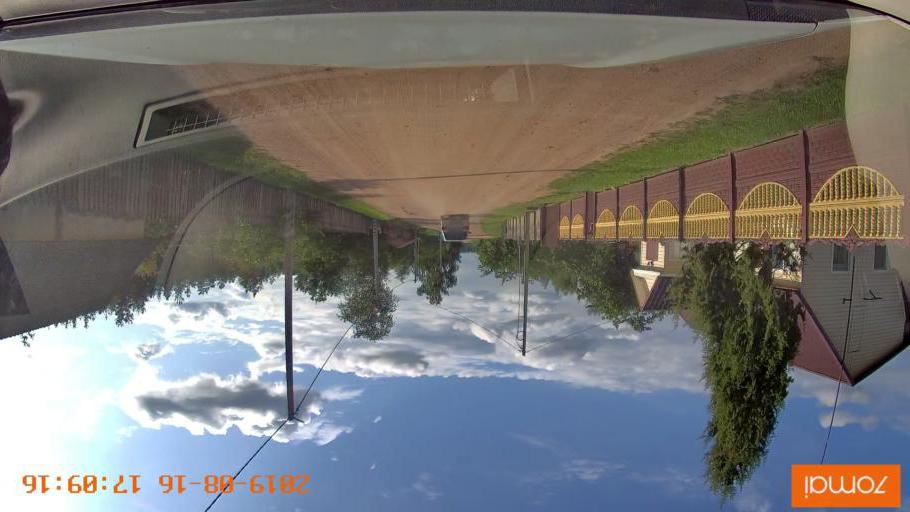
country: BY
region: Mogilev
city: Hlusha
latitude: 53.2149
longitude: 28.9252
